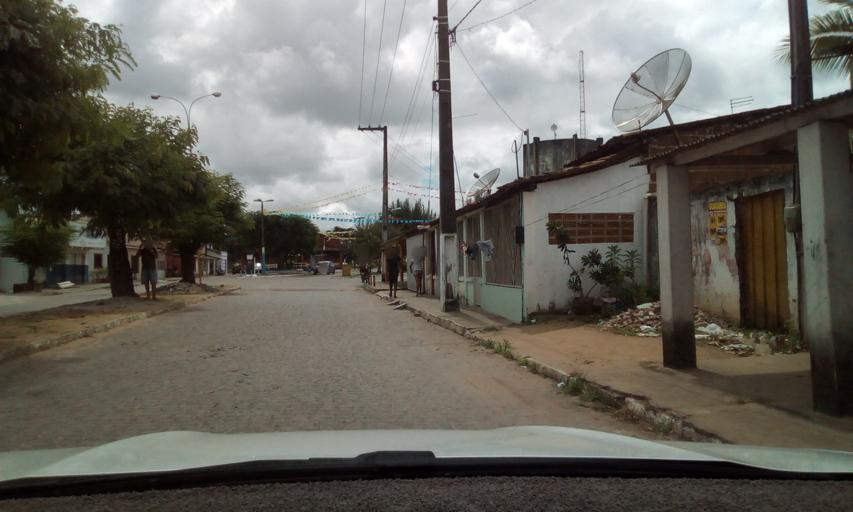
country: BR
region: Paraiba
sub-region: Rio Tinto
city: Rio Tinto
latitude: -6.7873
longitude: -35.0661
